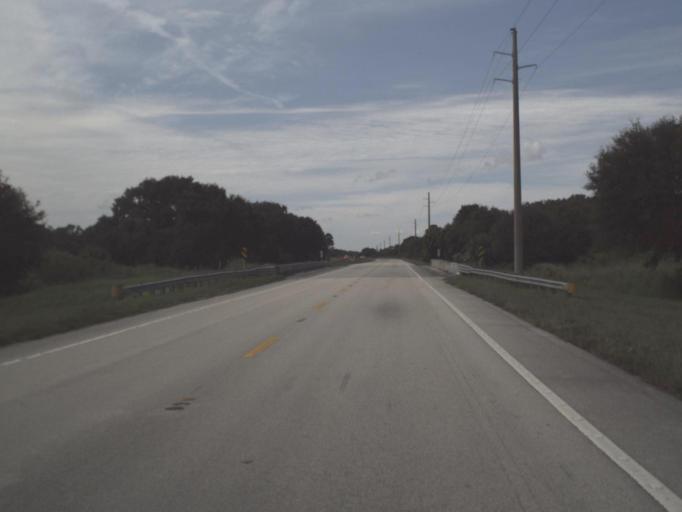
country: US
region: Florida
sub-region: Highlands County
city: Placid Lakes
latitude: 27.2092
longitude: -81.4608
